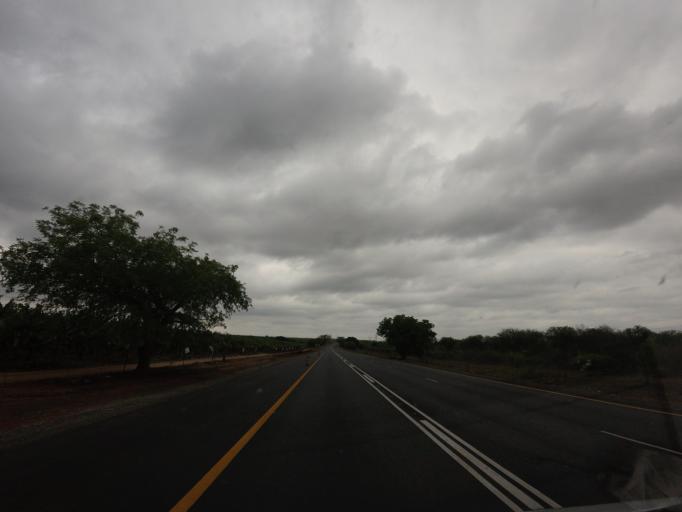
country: ZA
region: Mpumalanga
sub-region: Ehlanzeni District
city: Komatipoort
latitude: -25.4359
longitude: 31.8145
